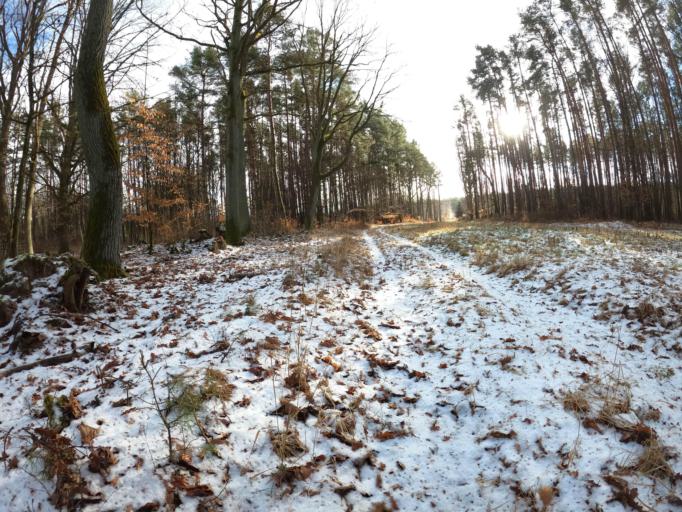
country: PL
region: Lubusz
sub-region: Powiat slubicki
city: Rzepin
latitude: 52.2958
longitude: 14.8148
